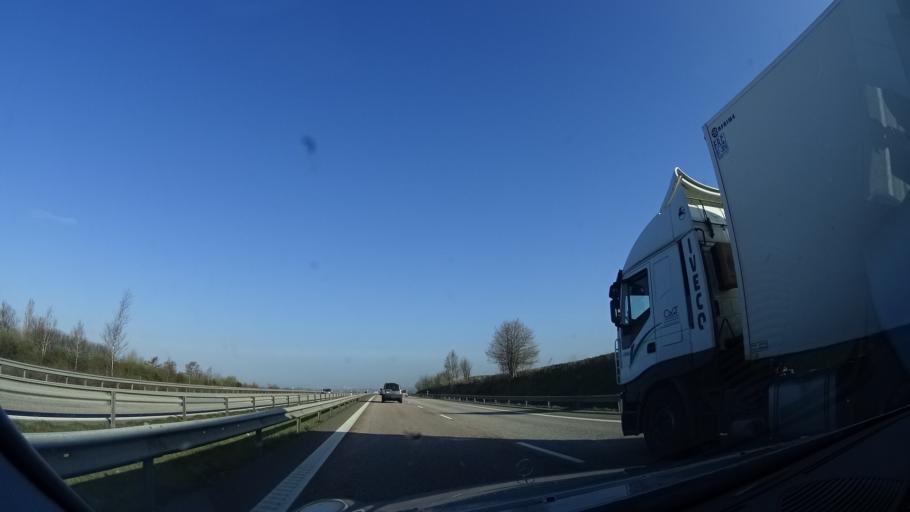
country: SE
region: Skane
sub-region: Helsingborg
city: Glumslov
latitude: 55.9471
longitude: 12.8115
